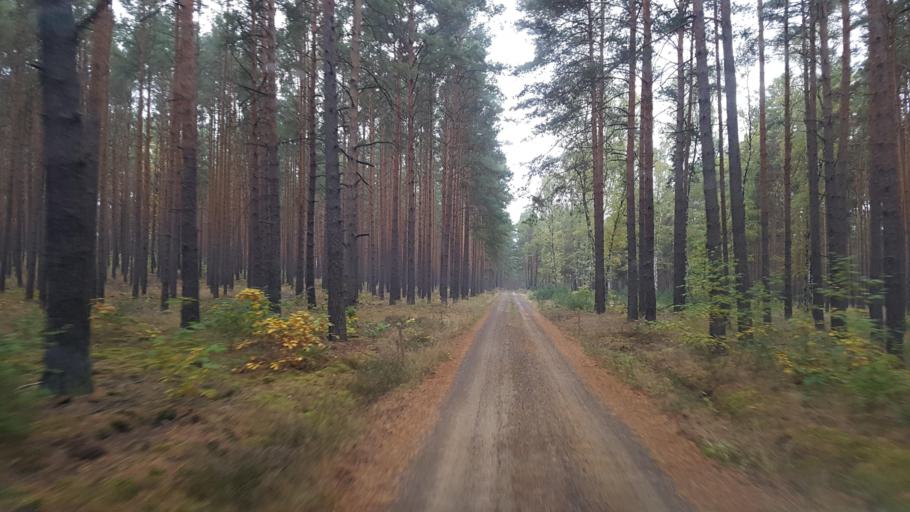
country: DE
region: Brandenburg
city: Schlieben
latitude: 51.7606
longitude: 13.4088
